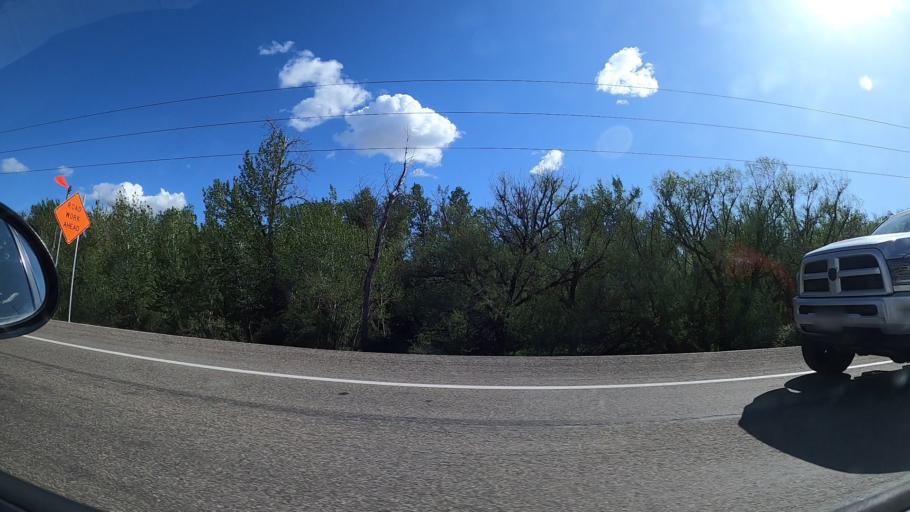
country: US
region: Idaho
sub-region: Ada County
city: Eagle
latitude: 43.6924
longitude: -116.3727
